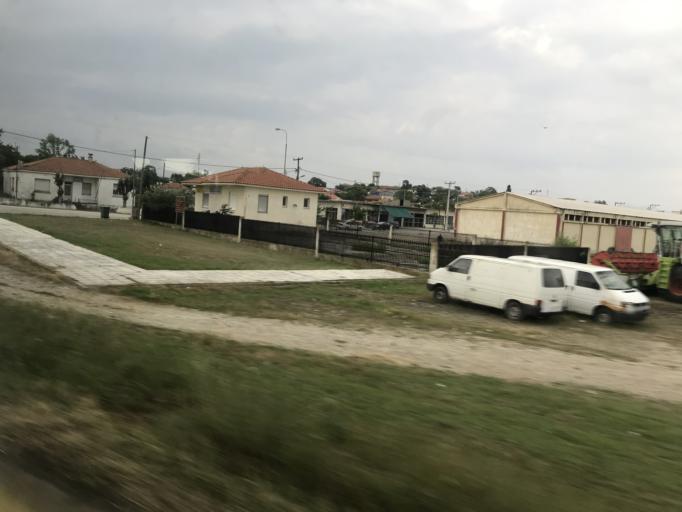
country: GR
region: East Macedonia and Thrace
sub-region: Nomos Rodopis
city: Arisvi
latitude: 41.0676
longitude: 25.5868
